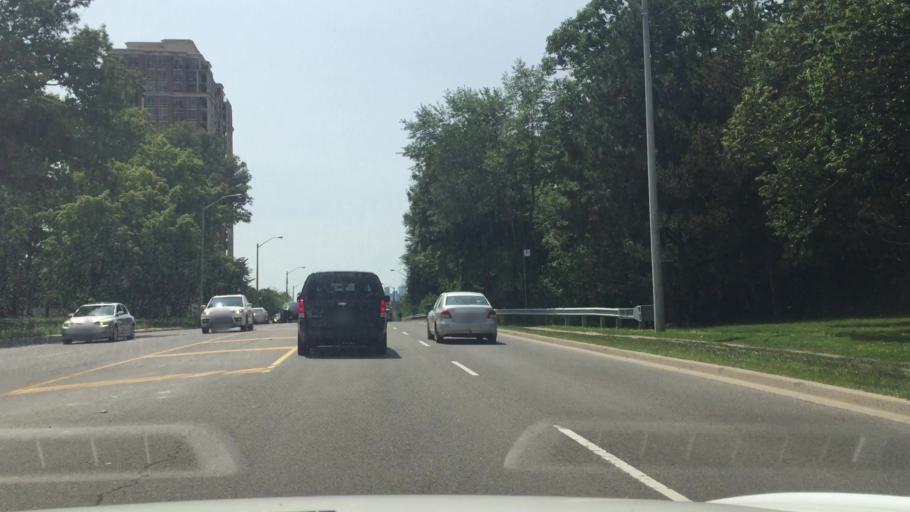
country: CA
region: Ontario
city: Willowdale
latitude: 43.7226
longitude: -79.3491
